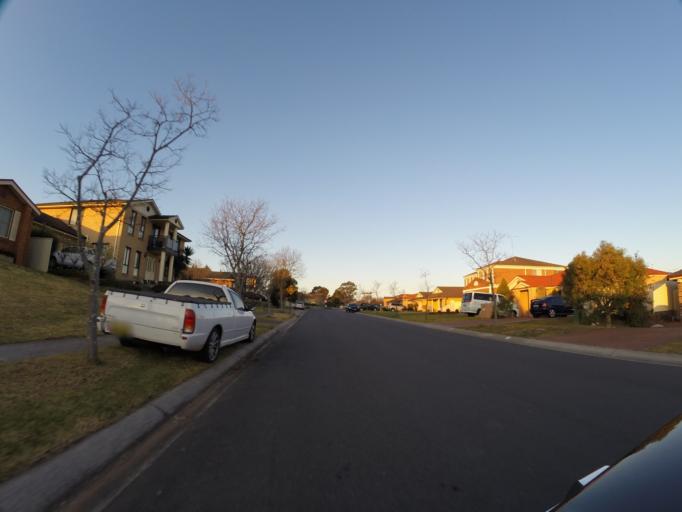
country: AU
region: New South Wales
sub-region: Camden
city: Narellan
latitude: -34.0235
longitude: 150.7310
